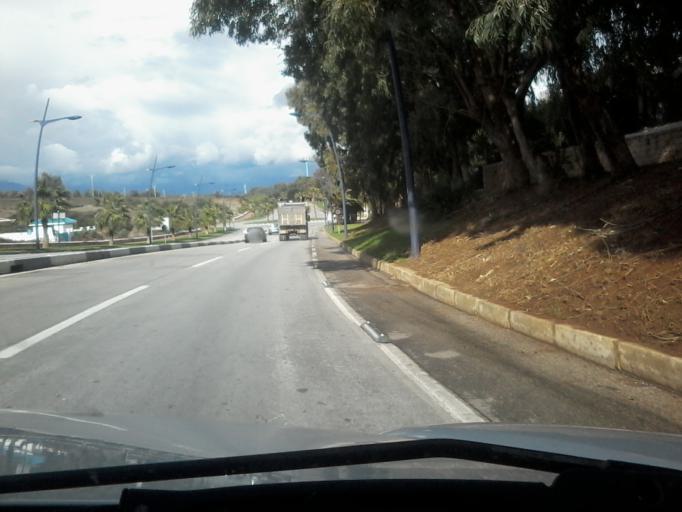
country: ES
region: Ceuta
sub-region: Ceuta
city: Ceuta
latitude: 35.7620
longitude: -5.3487
